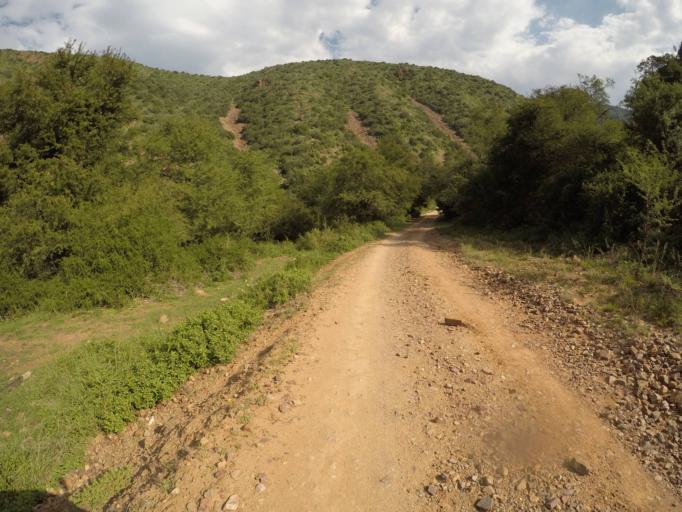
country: ZA
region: Eastern Cape
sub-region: Cacadu District Municipality
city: Kareedouw
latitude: -33.6421
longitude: 24.3171
